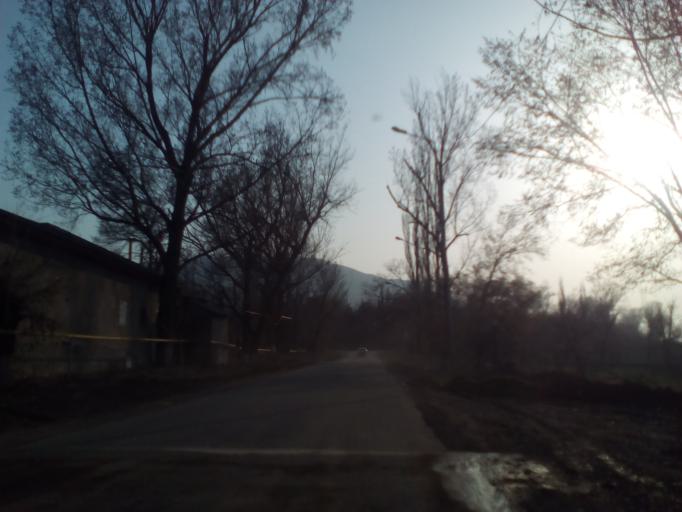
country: KZ
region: Almaty Oblysy
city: Burunday
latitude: 43.1612
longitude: 76.4558
